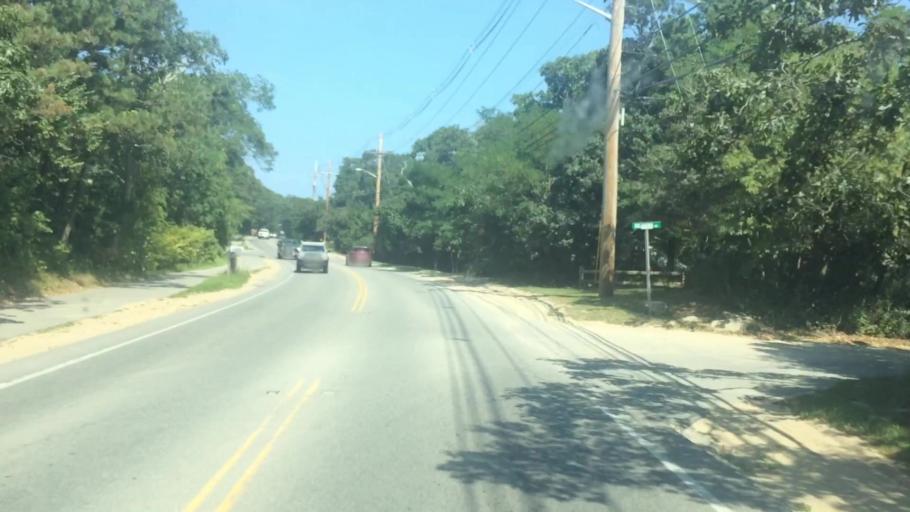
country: US
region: Massachusetts
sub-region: Dukes County
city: Vineyard Haven
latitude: 41.4393
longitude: -70.6083
